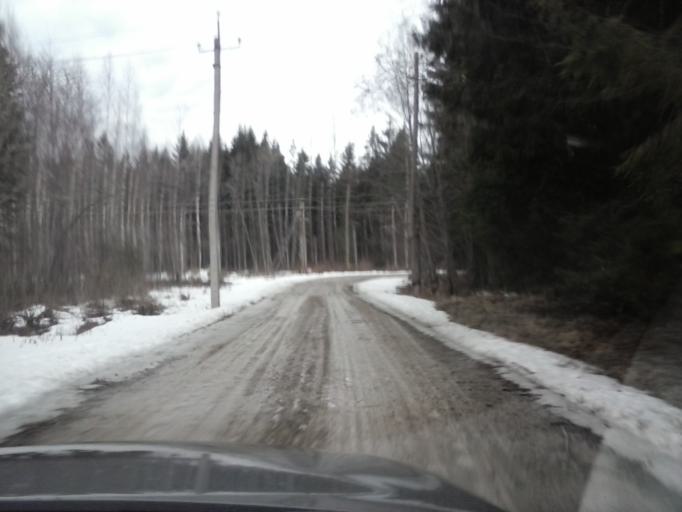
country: EE
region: Ida-Virumaa
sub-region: Johvi vald
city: Johvi
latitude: 59.1798
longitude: 27.3281
